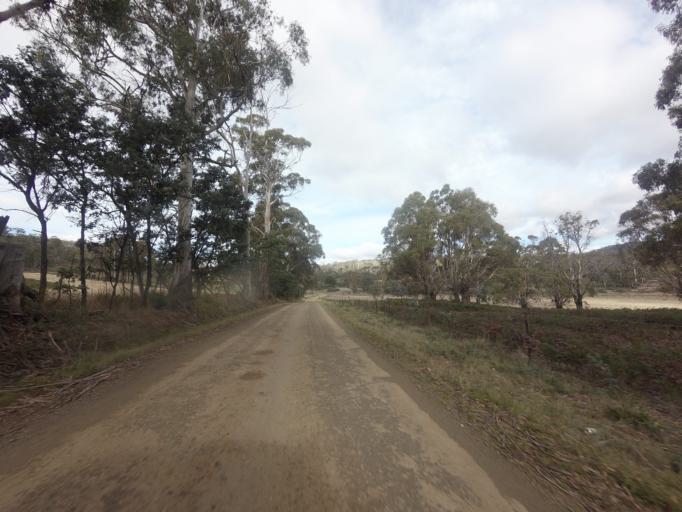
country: AU
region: Tasmania
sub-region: Brighton
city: Bridgewater
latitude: -42.4853
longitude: 147.3034
